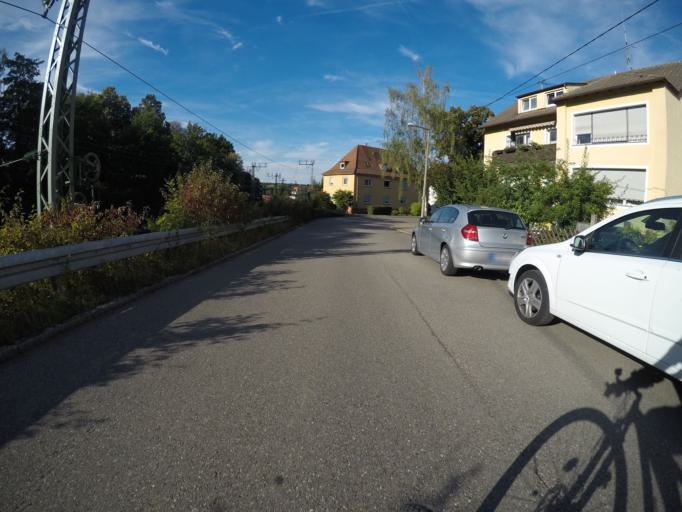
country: DE
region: Baden-Wuerttemberg
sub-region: Regierungsbezirk Stuttgart
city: Leinfelden-Echterdingen
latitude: 48.7315
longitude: 9.1196
